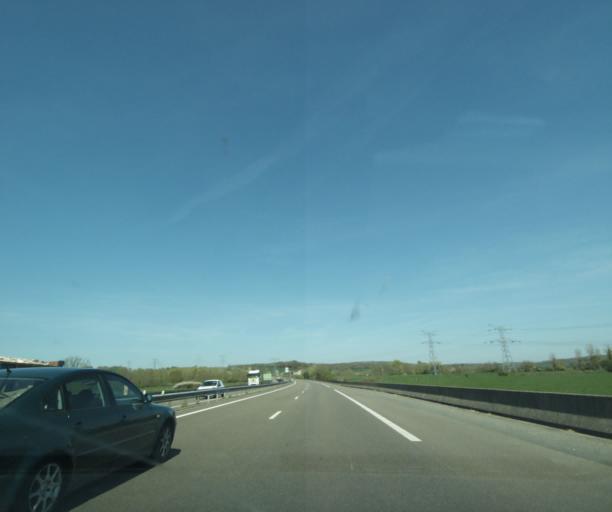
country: FR
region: Bourgogne
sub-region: Departement de la Nievre
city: Coulanges-les-Nevers
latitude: 47.0051
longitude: 3.2048
